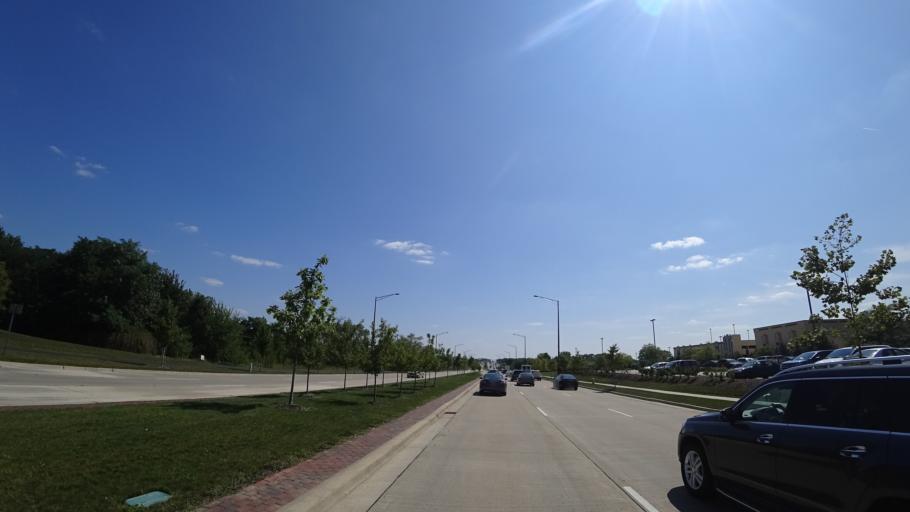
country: US
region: Illinois
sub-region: Cook County
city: Orland Hills
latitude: 41.5925
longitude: -87.8526
